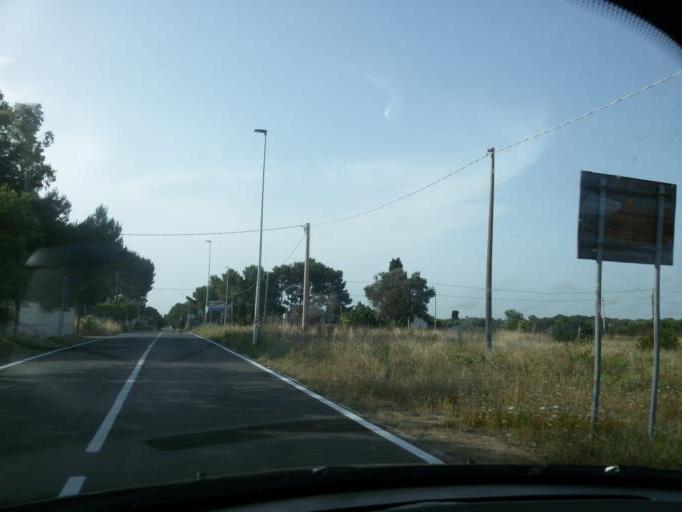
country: IT
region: Apulia
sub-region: Provincia di Lecce
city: Porto Cesareo
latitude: 40.2399
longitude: 17.9160
